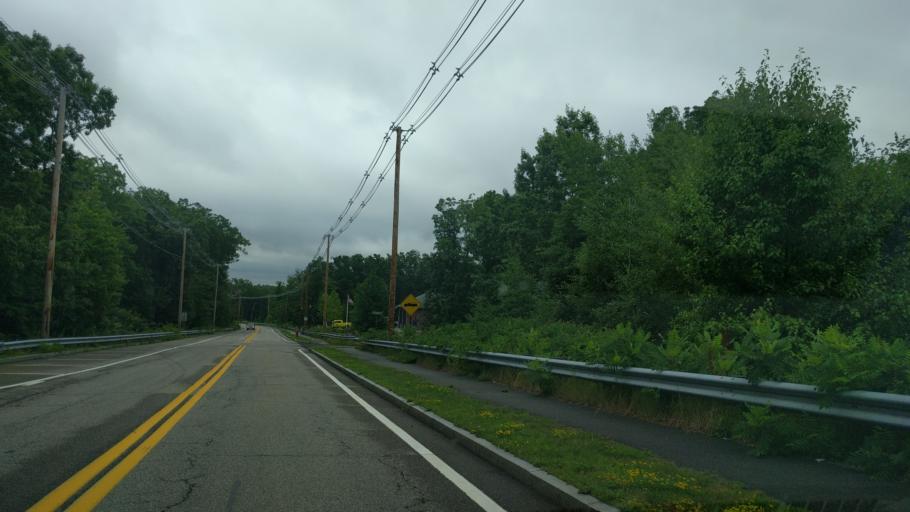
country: US
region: Massachusetts
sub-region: Worcester County
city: Shrewsbury
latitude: 42.2610
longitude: -71.6950
